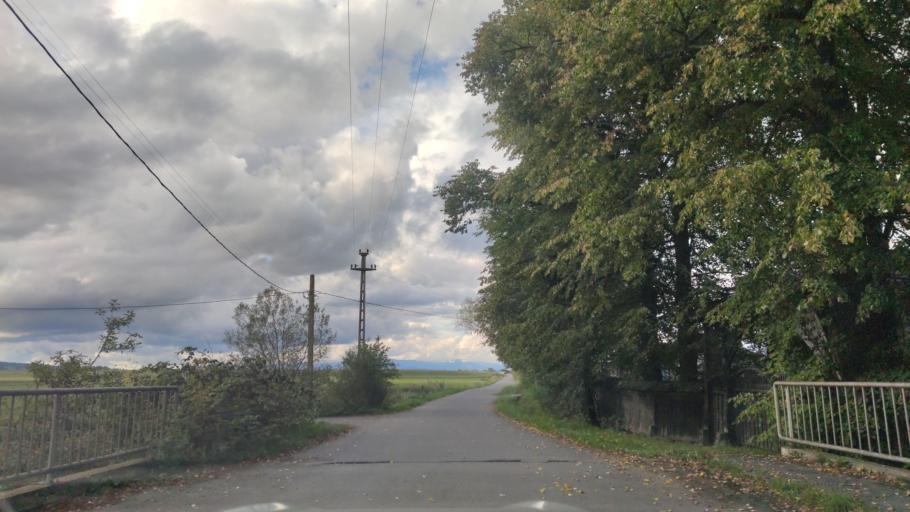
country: RO
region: Harghita
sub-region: Comuna Remetea
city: Remetea
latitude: 46.8108
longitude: 25.4363
